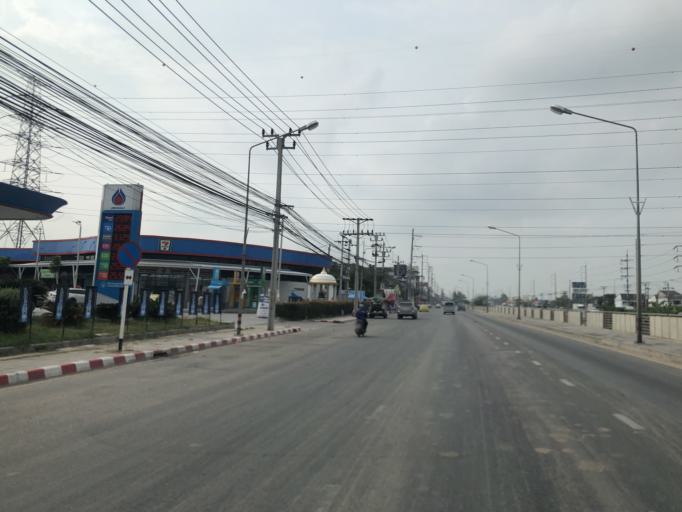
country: TH
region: Bangkok
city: Bang Na
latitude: 13.5962
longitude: 100.6991
